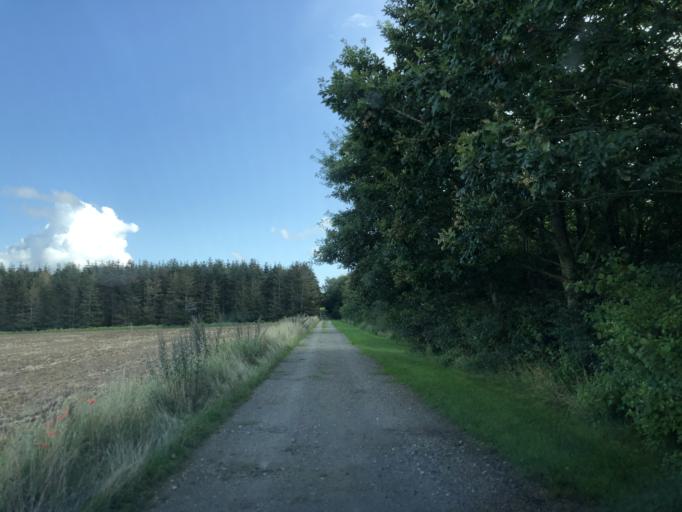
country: DK
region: Central Jutland
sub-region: Favrskov Kommune
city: Hadsten
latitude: 56.3208
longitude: 10.0203
